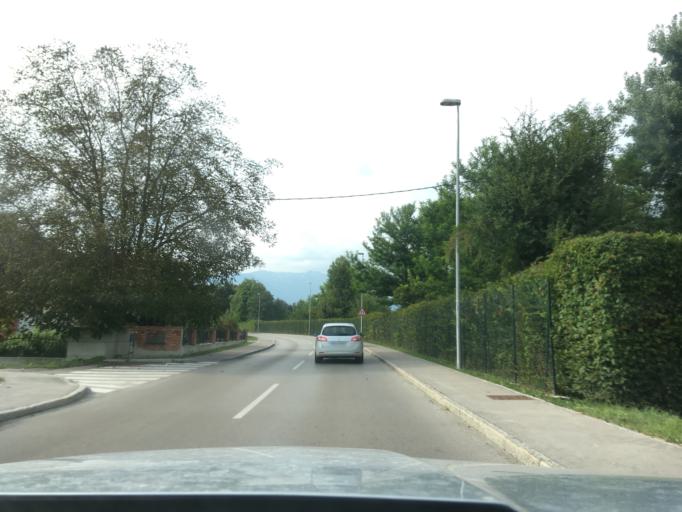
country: SI
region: Domzale
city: Radomlje
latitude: 46.1823
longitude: 14.6085
